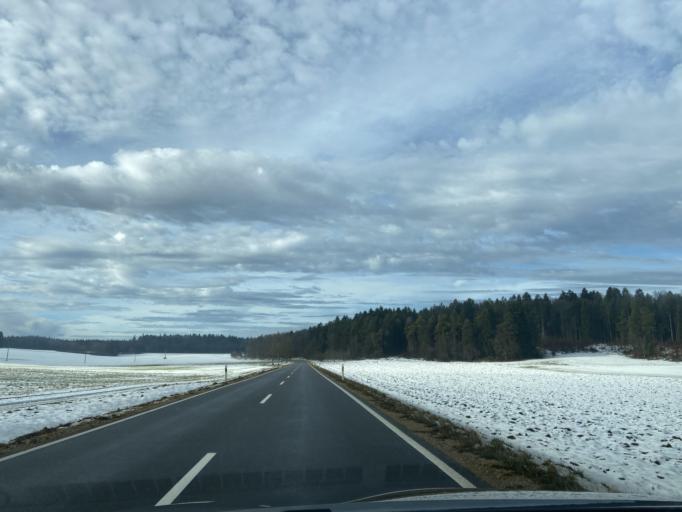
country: DE
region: Baden-Wuerttemberg
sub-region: Tuebingen Region
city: Pfronstetten
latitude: 48.2432
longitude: 9.3059
